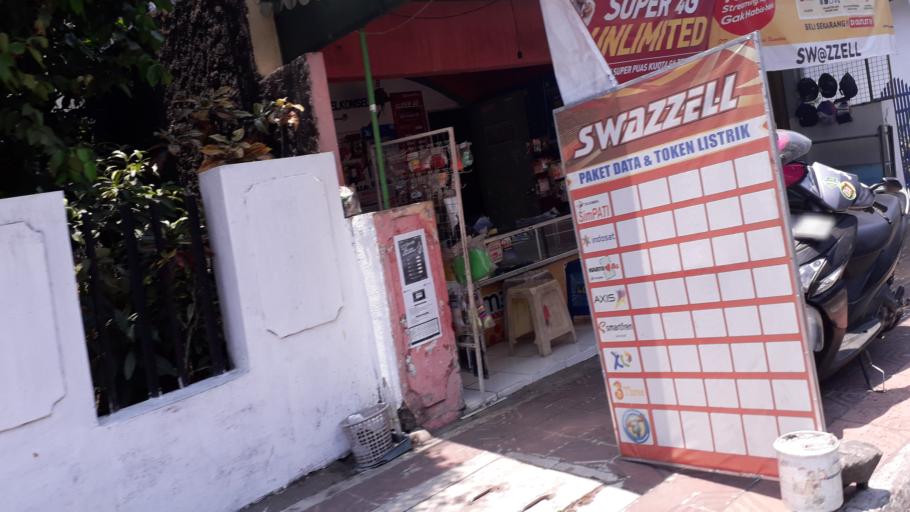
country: ID
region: Daerah Istimewa Yogyakarta
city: Yogyakarta
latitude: -7.7640
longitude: 110.3693
